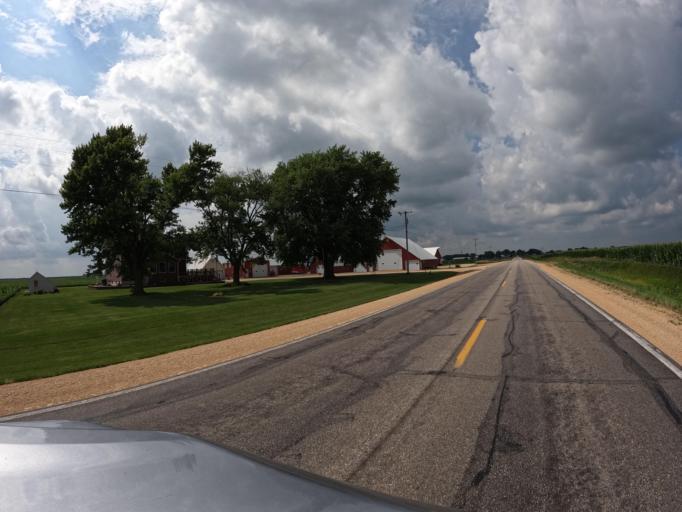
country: US
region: Iowa
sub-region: Clinton County
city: Camanche
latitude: 41.7908
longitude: -90.3549
